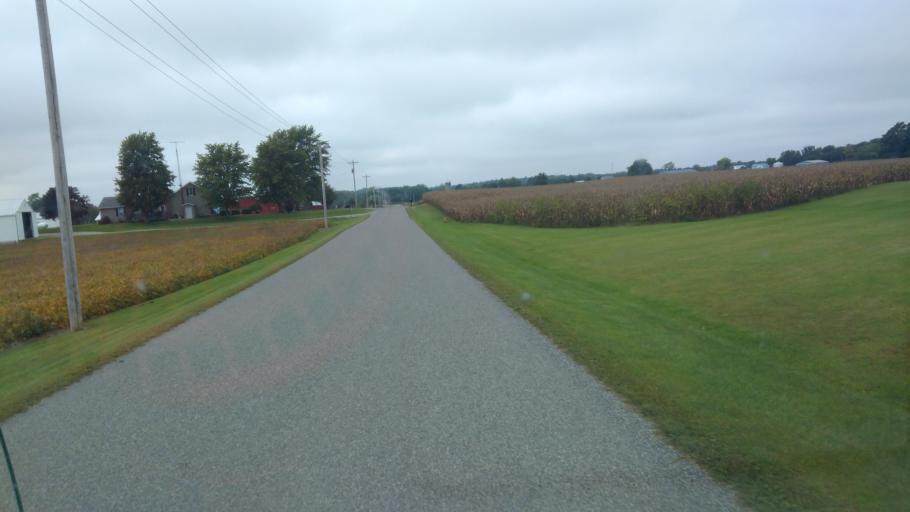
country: US
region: Ohio
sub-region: Hardin County
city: Kenton
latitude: 40.5743
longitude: -83.6574
